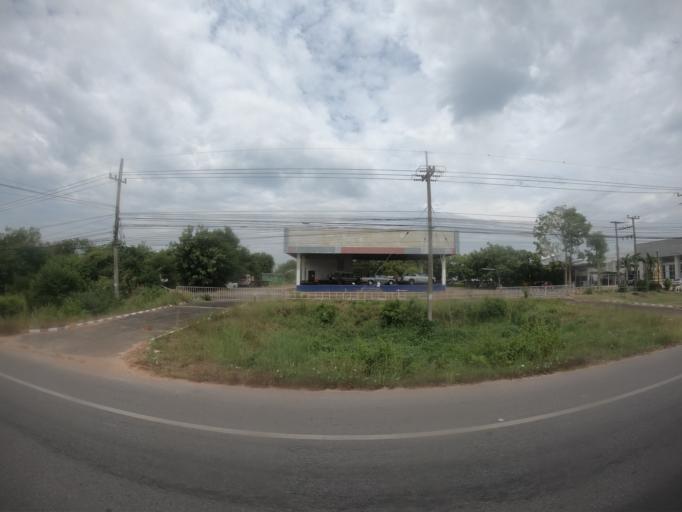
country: TH
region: Maha Sarakham
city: Maha Sarakham
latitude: 16.1629
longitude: 103.3443
